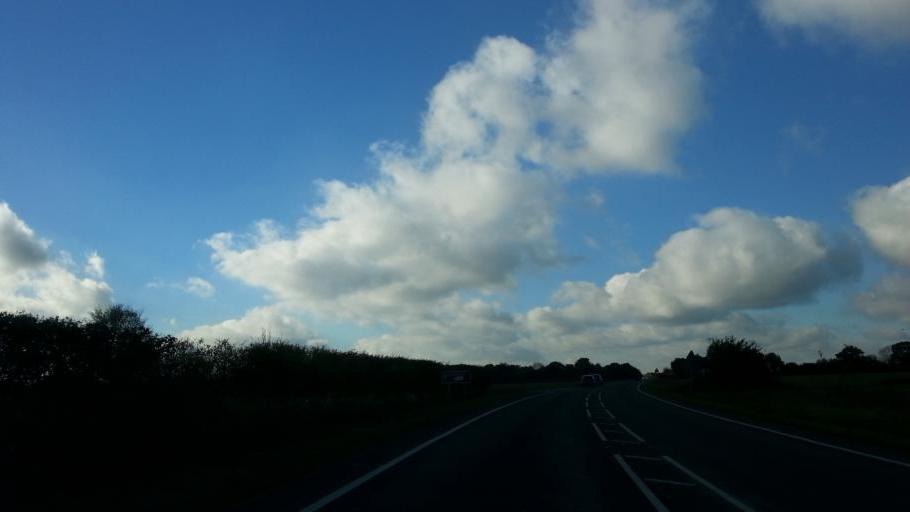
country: GB
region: England
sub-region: Suffolk
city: Beccles
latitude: 52.4831
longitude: 1.5241
